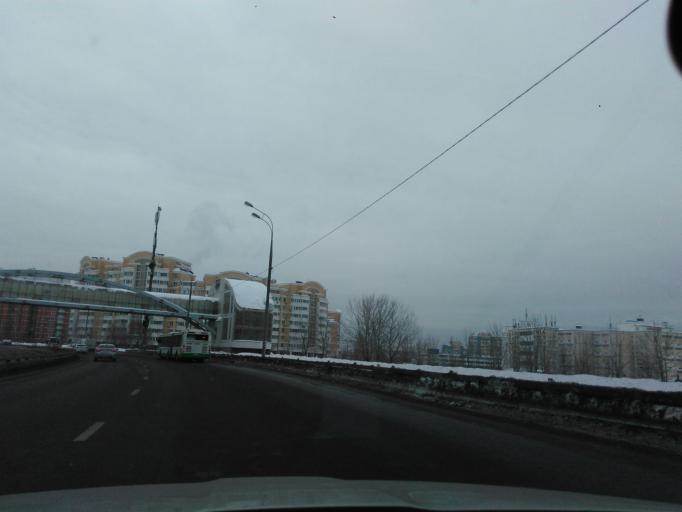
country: RU
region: Moscow
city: Khimki
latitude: 55.9029
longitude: 37.3904
